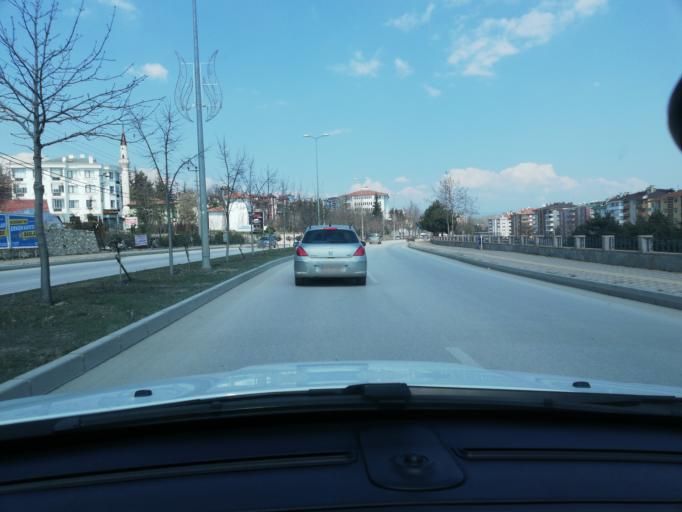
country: TR
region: Kastamonu
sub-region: Cide
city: Kastamonu
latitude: 41.4001
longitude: 33.7810
